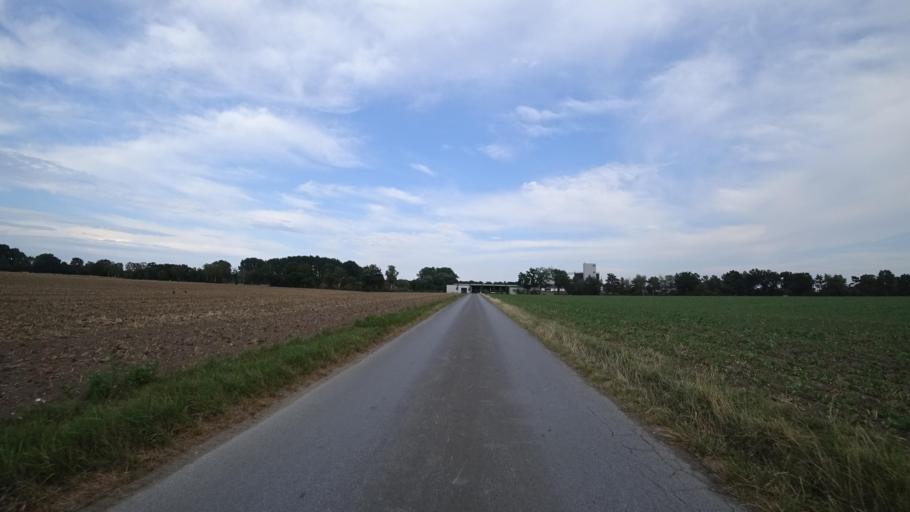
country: DE
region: North Rhine-Westphalia
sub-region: Regierungsbezirk Detmold
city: Rheda-Wiedenbruck
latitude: 51.8706
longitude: 8.2933
